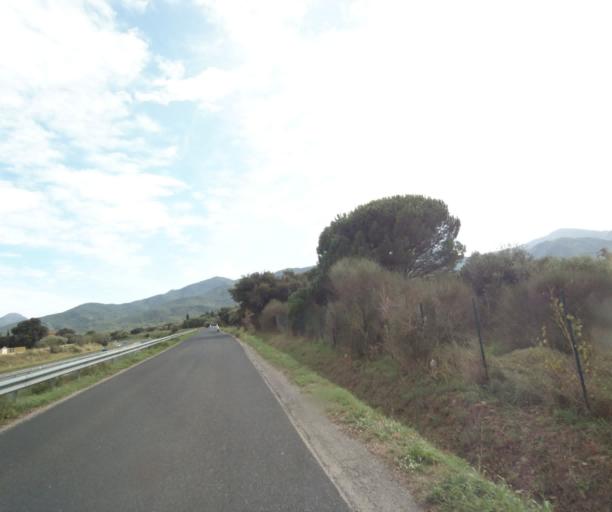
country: FR
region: Languedoc-Roussillon
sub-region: Departement des Pyrenees-Orientales
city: Argelers
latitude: 42.5483
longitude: 3.0062
